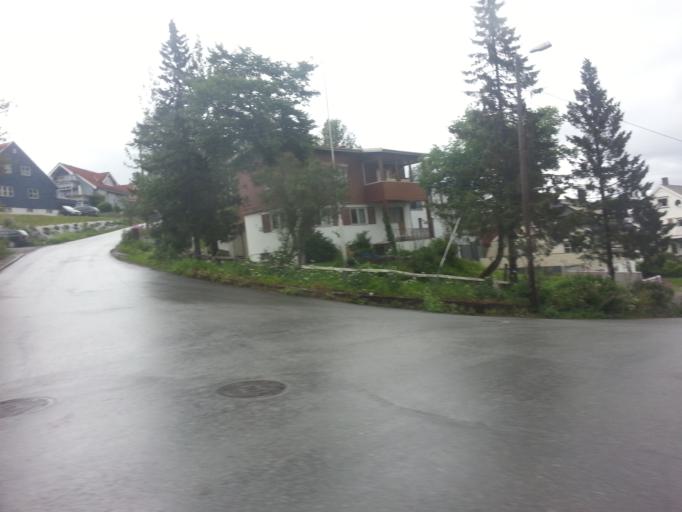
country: NO
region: Troms
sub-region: Tromso
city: Tromso
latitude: 69.6564
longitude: 18.9488
